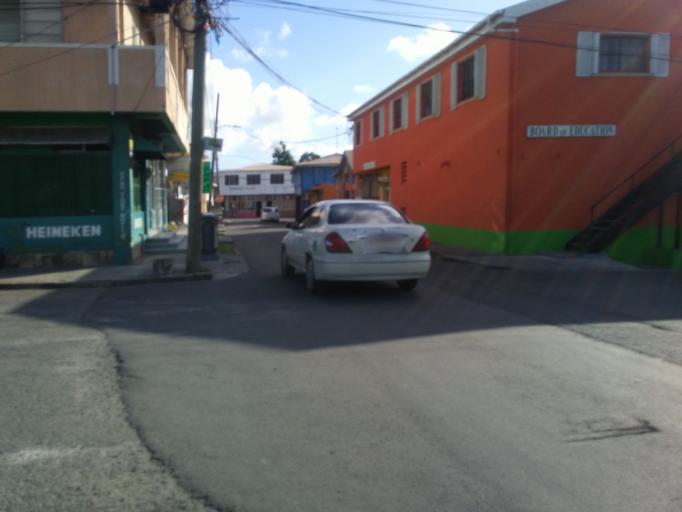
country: AG
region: Saint John
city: Saint John's
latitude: 17.1238
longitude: -61.8447
